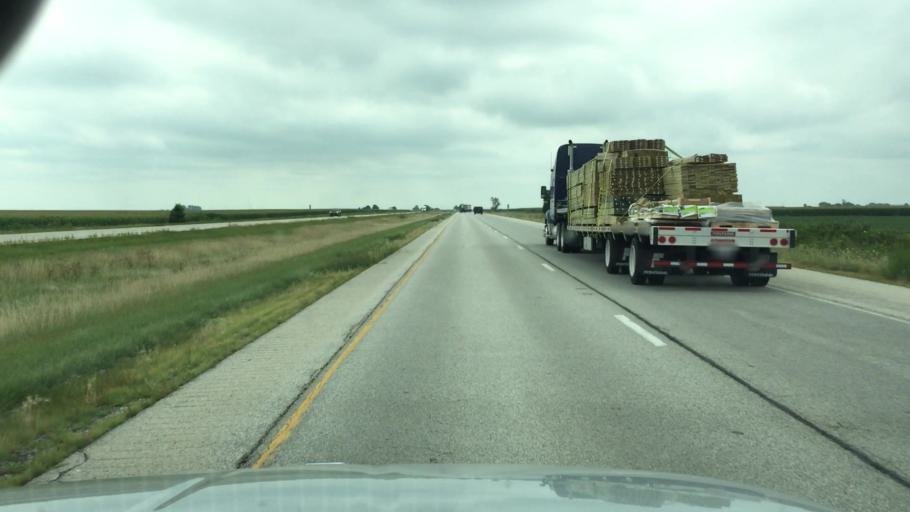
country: US
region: Illinois
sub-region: Knox County
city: Galesburg
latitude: 41.0508
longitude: -90.3342
